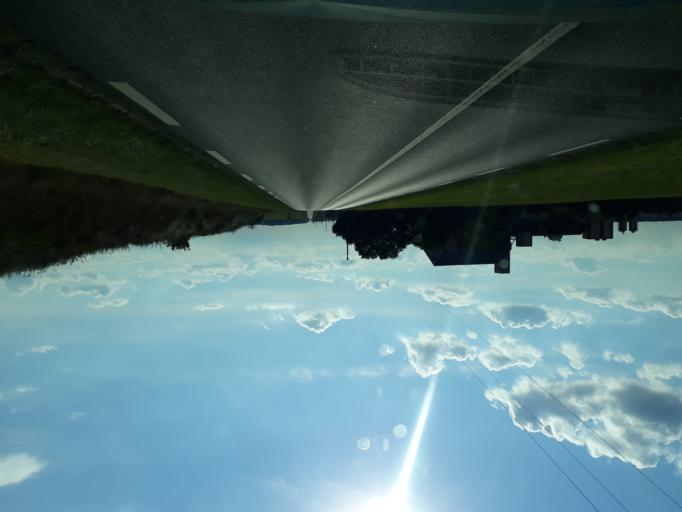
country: FR
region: Centre
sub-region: Departement du Loir-et-Cher
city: Oucques
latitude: 47.9042
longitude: 1.3830
